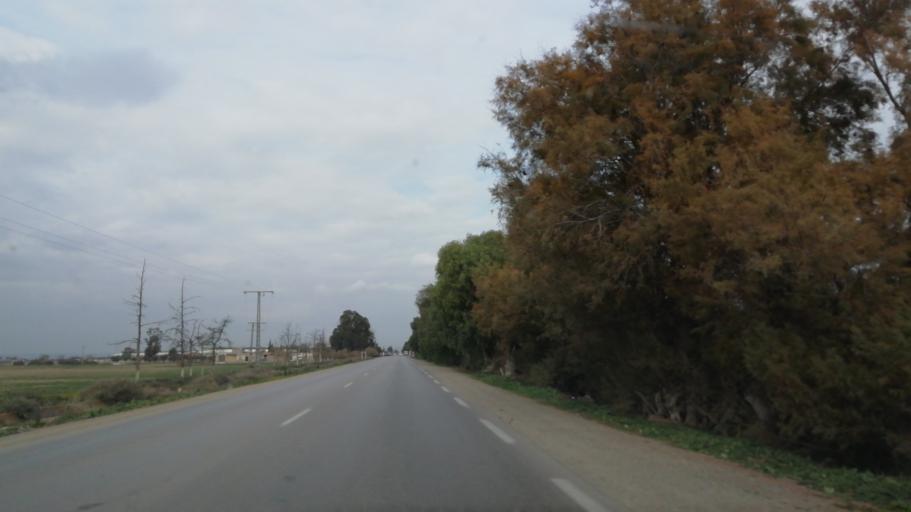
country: DZ
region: Mascara
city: Mascara
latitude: 35.6518
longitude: 0.0594
